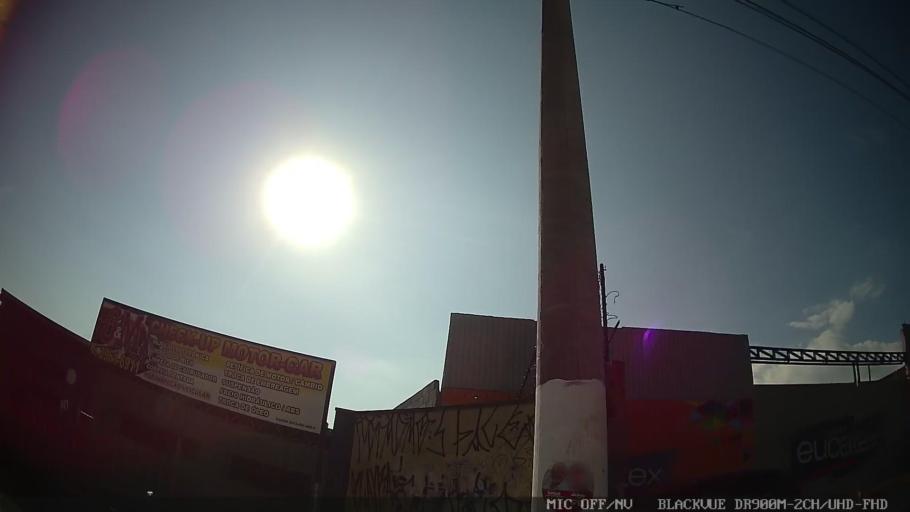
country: BR
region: Sao Paulo
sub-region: Ferraz De Vasconcelos
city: Ferraz de Vasconcelos
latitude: -23.5400
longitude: -46.4085
